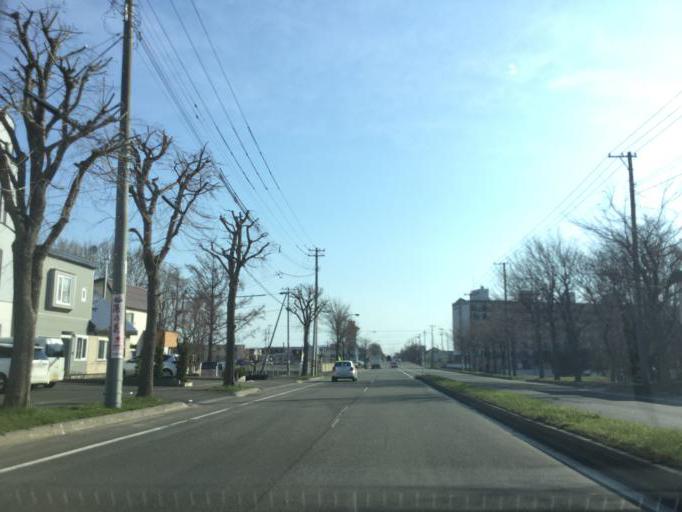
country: JP
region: Hokkaido
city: Ebetsu
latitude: 43.0896
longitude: 141.5057
